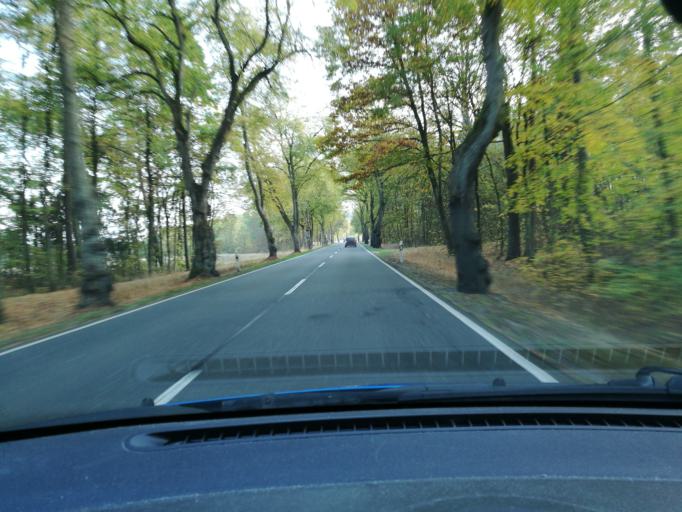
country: DE
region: Lower Saxony
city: Karwitz
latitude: 53.1101
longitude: 11.0180
